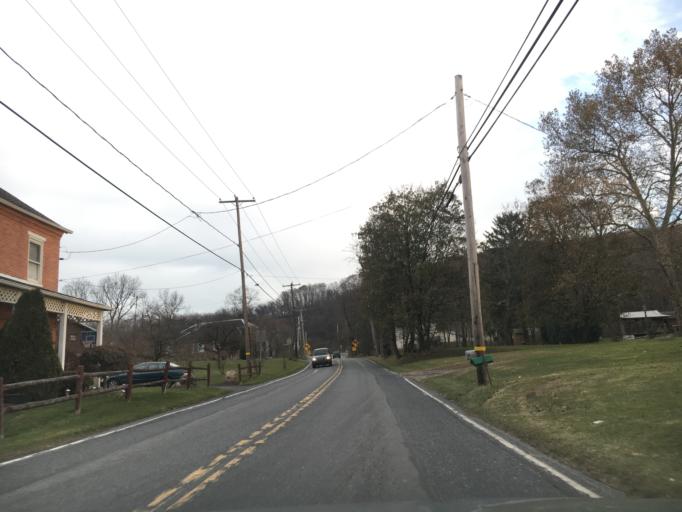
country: US
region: Pennsylvania
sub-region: Lehigh County
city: Slatington
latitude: 40.7234
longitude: -75.6149
